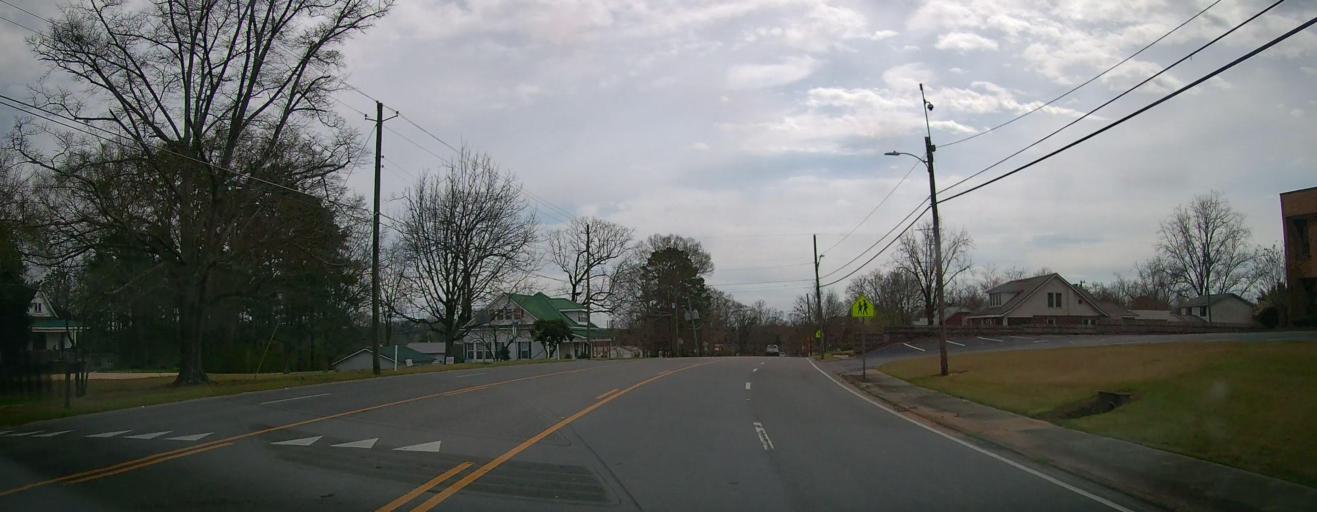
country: US
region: Alabama
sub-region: Marion County
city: Guin
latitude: 33.9739
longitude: -87.9151
